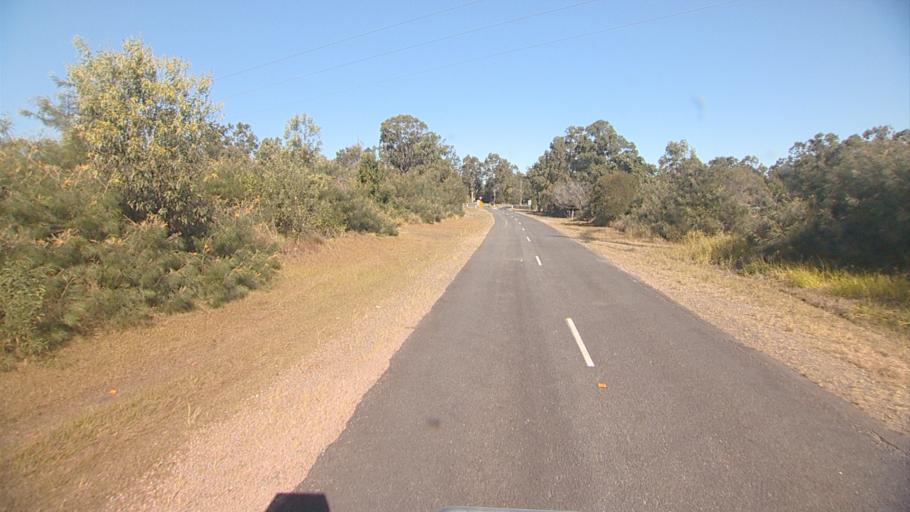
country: AU
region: Queensland
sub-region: Logan
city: North Maclean
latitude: -27.7334
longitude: 152.9606
